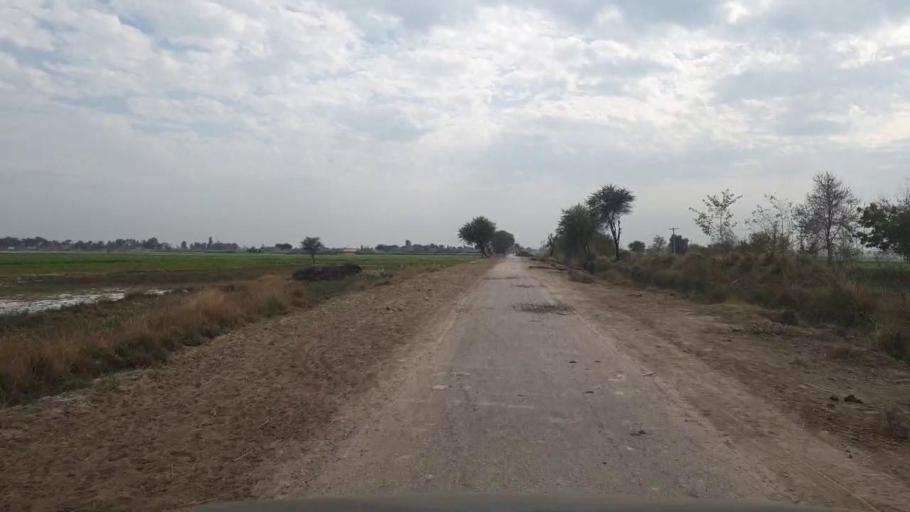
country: PK
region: Sindh
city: Hala
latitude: 26.0121
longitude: 68.4322
